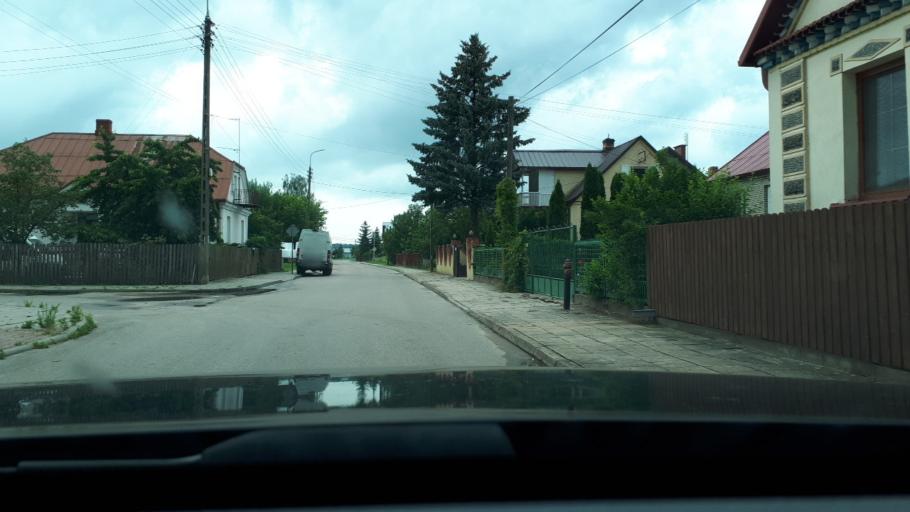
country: PL
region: Podlasie
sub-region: Powiat moniecki
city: Knyszyn
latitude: 53.3130
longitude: 22.9138
